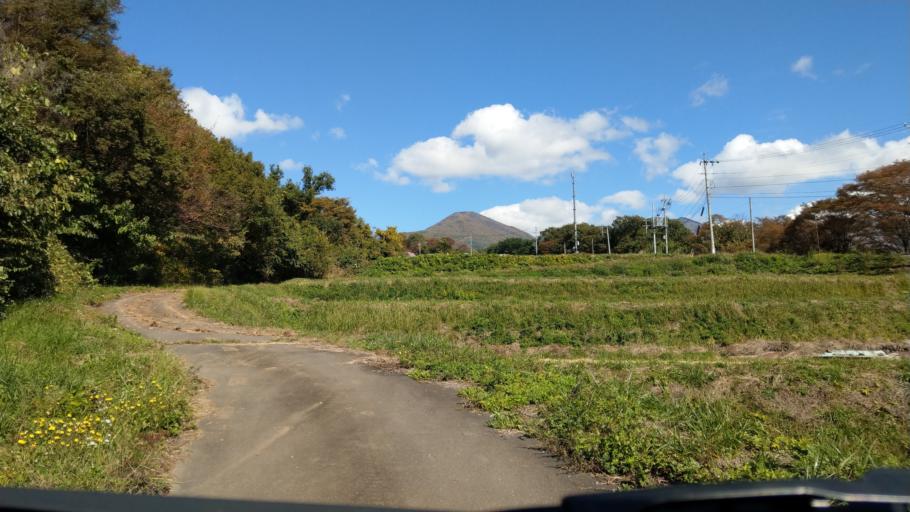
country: JP
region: Nagano
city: Komoro
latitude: 36.3530
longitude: 138.4221
